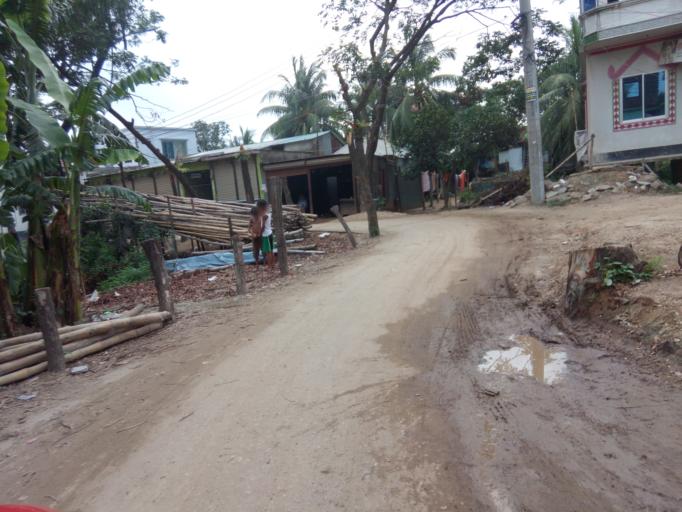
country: BD
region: Dhaka
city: Paltan
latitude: 23.7441
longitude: 90.4616
